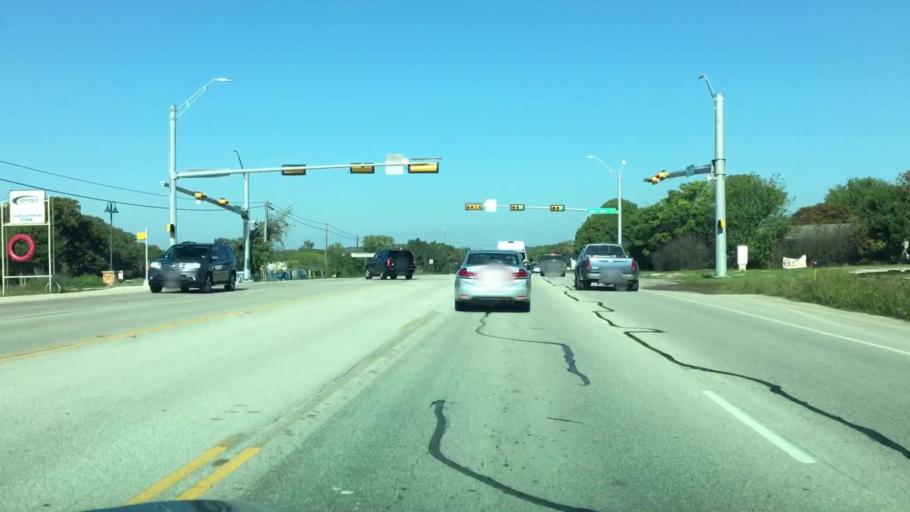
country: US
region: Texas
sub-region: Hays County
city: Dripping Springs
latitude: 30.1966
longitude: -98.1050
